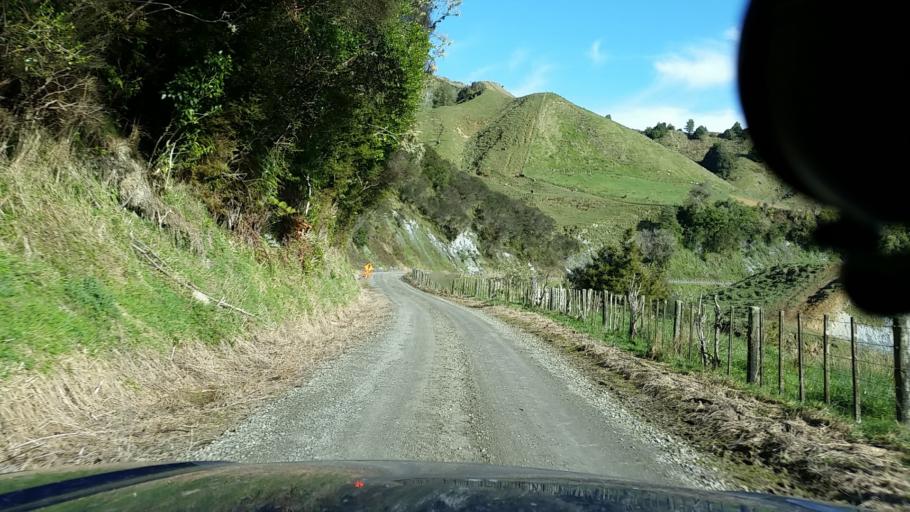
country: NZ
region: Taranaki
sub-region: New Plymouth District
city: Waitara
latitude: -39.0521
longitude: 174.7547
